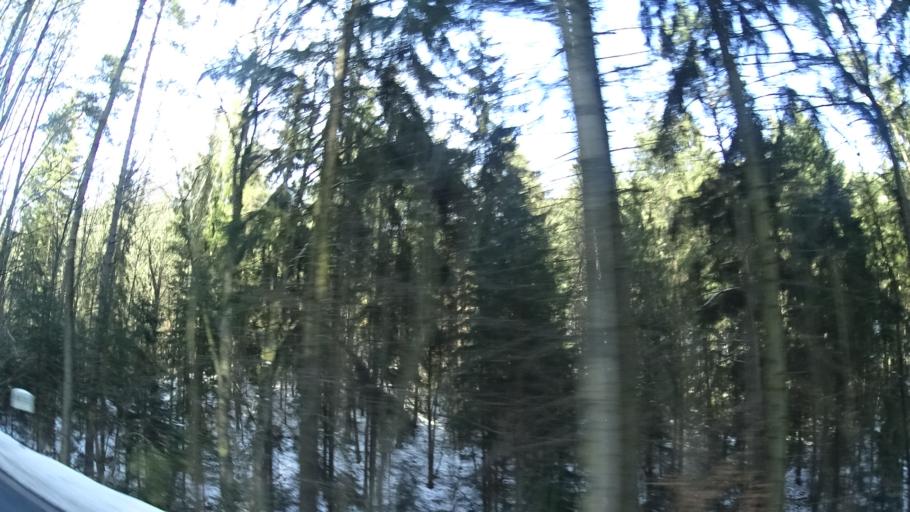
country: DE
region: Thuringia
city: Altenberga
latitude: 50.8508
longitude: 11.5402
